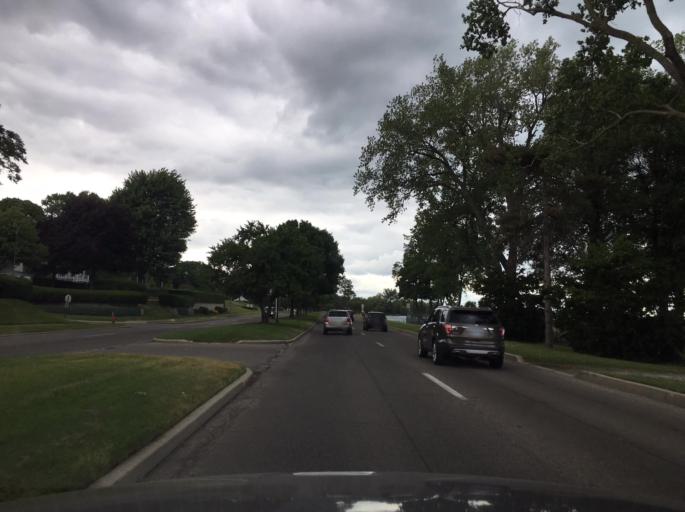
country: US
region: Michigan
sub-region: Wayne County
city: Grosse Pointe Farms
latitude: 42.3976
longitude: -82.8890
